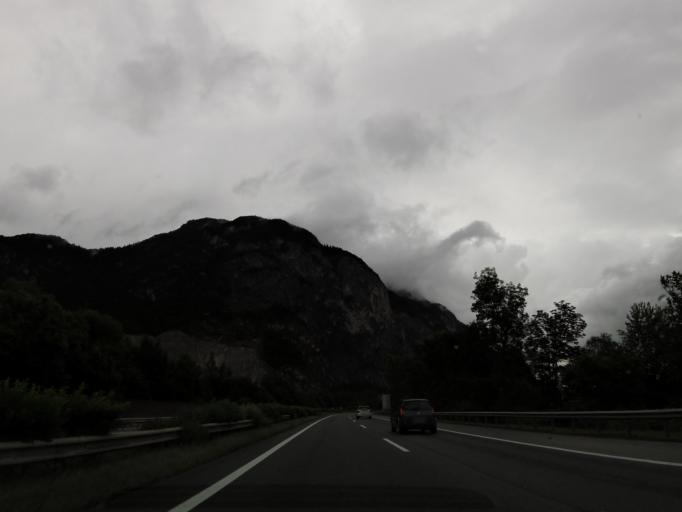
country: AT
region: Tyrol
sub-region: Politischer Bezirk Innsbruck Land
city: Unterperfuss
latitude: 47.2630
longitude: 11.2540
